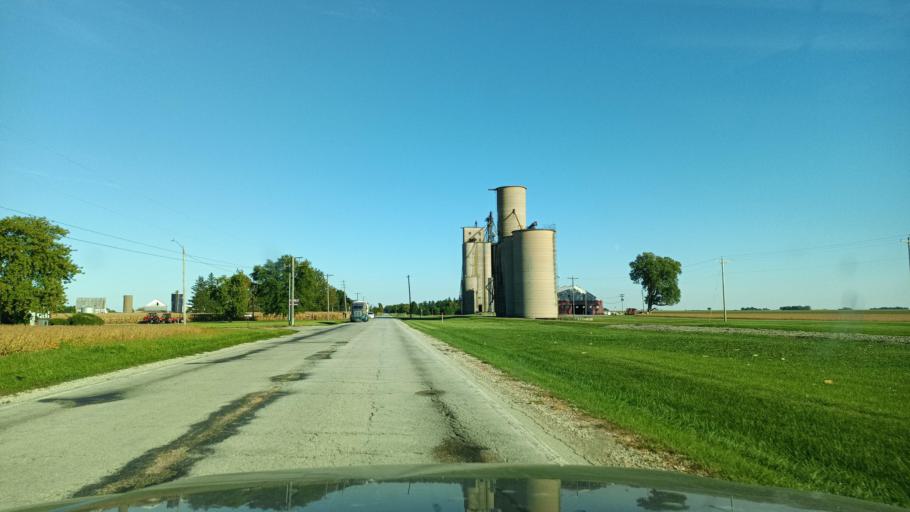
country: US
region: Illinois
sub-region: De Witt County
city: Farmer City
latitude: 40.2337
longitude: -88.5964
